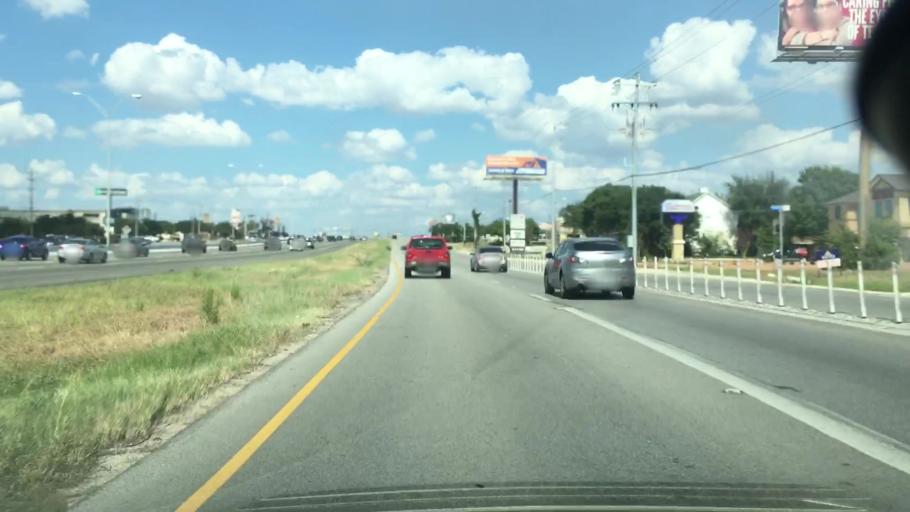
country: US
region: Texas
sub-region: Bexar County
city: Selma
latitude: 29.5933
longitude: -98.2886
